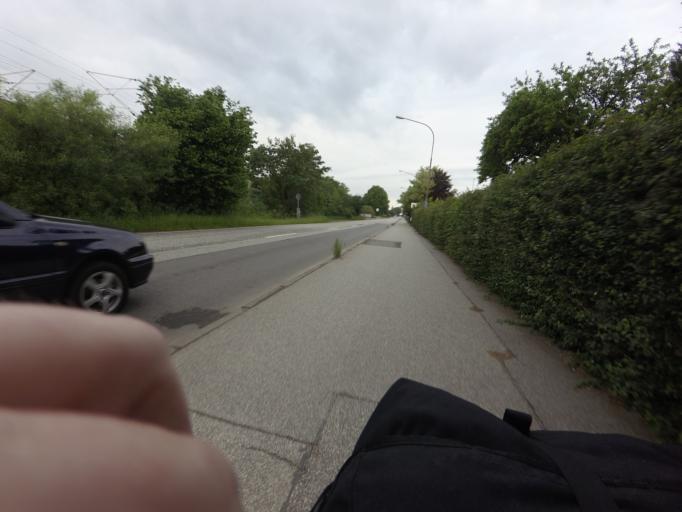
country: DE
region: Schleswig-Holstein
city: Ratekau
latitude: 53.9121
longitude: 10.7496
